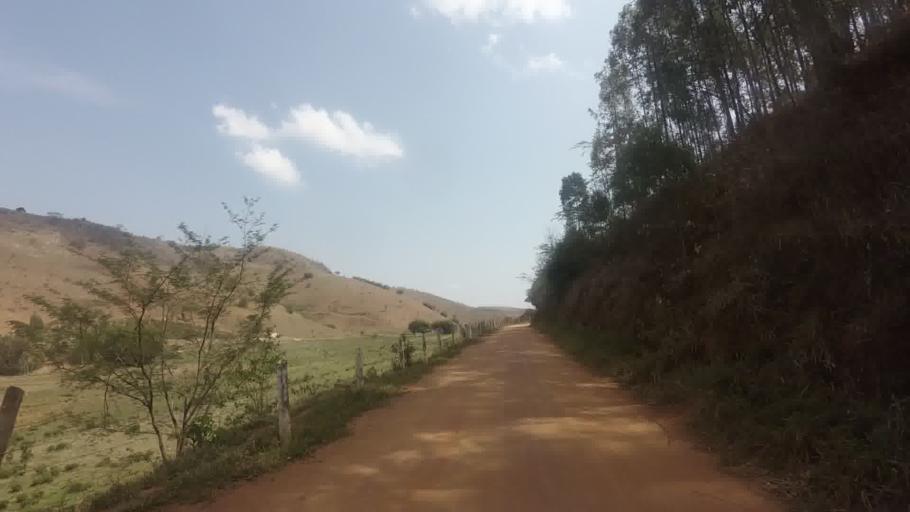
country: BR
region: Espirito Santo
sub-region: Sao Jose Do Calcado
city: Sao Jose do Calcado
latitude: -21.0519
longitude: -41.5289
